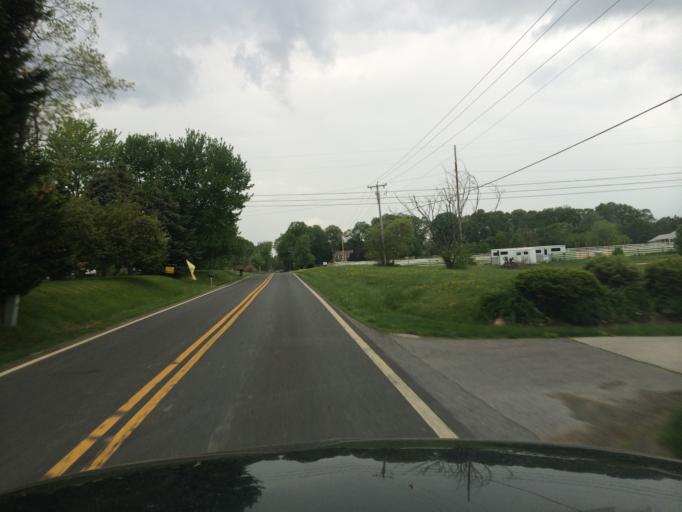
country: US
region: Maryland
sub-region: Carroll County
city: Eldersburg
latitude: 39.4432
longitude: -76.9810
